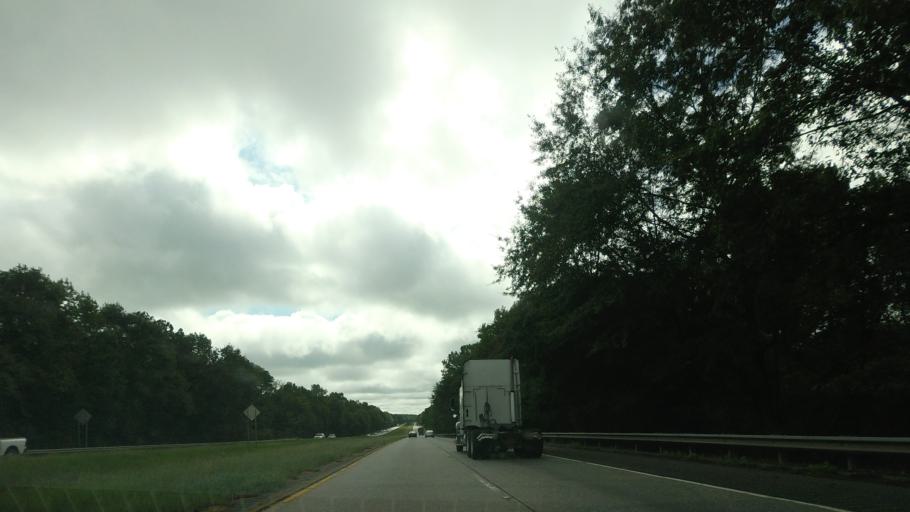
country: US
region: Georgia
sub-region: Bibb County
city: Macon
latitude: 32.8239
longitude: -83.5969
